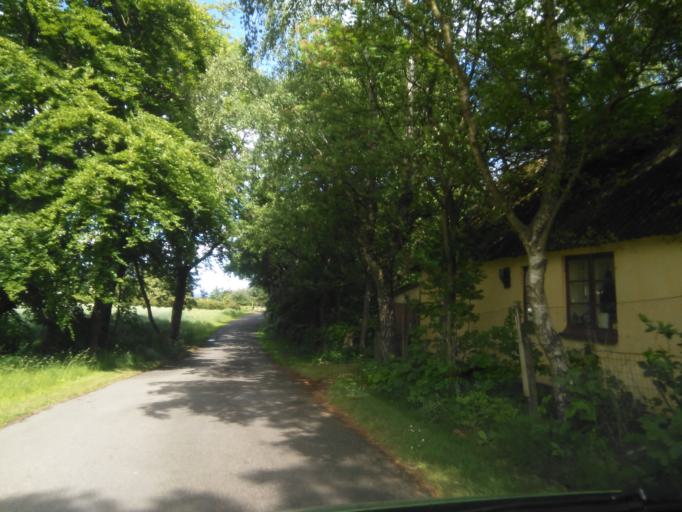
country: DK
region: Capital Region
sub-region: Bornholm Kommune
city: Nexo
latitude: 55.0973
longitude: 15.1178
